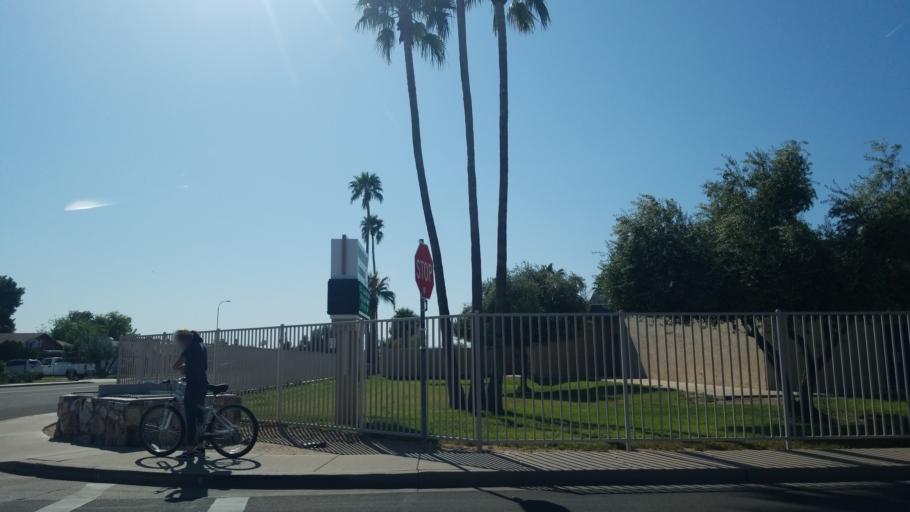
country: US
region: Arizona
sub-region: Maricopa County
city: Glendale
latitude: 33.5605
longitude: -112.1777
